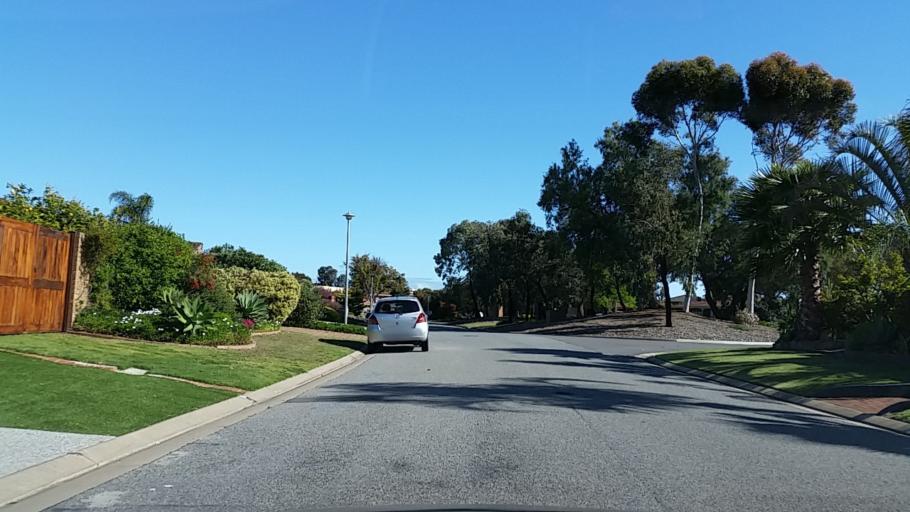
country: AU
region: South Australia
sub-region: Charles Sturt
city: West Lakes Shore
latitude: -34.8685
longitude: 138.4924
